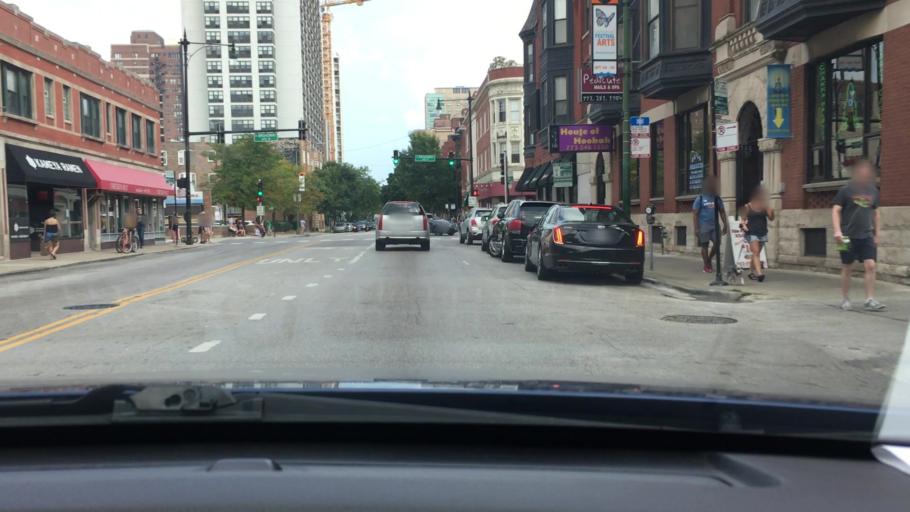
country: US
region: Illinois
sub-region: Cook County
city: Chicago
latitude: 41.9400
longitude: -87.6451
